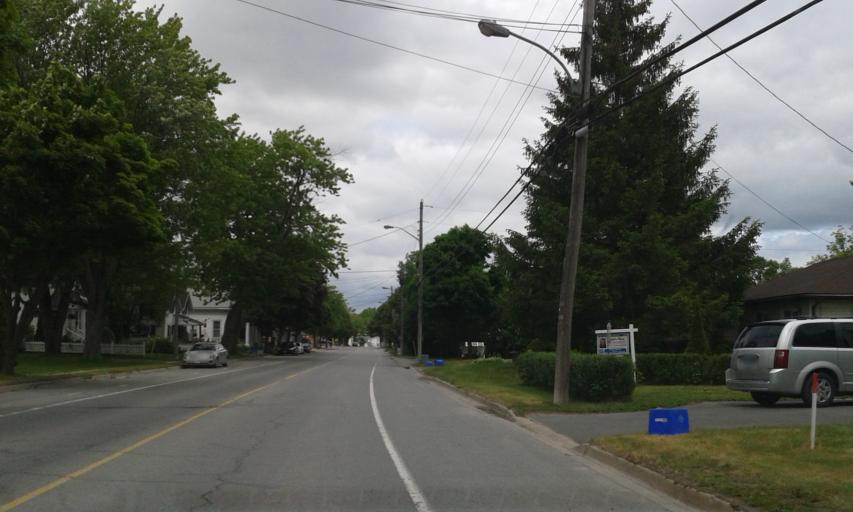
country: CA
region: Ontario
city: Skatepark
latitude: 44.1797
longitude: -76.7813
